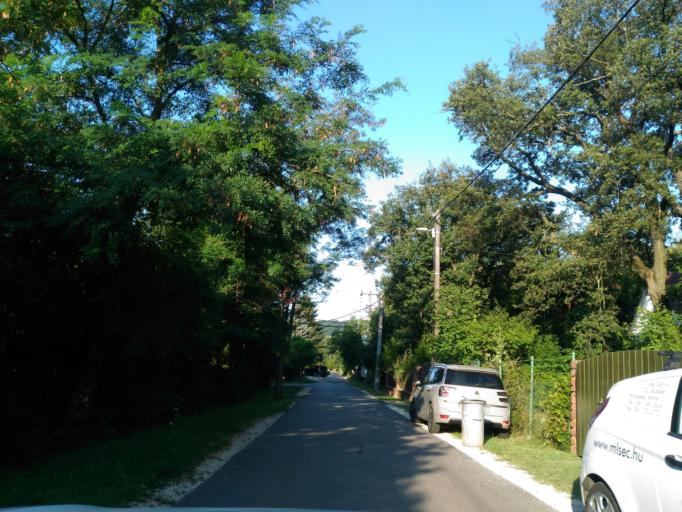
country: HU
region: Veszprem
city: Zanka
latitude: 46.8523
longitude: 17.6560
